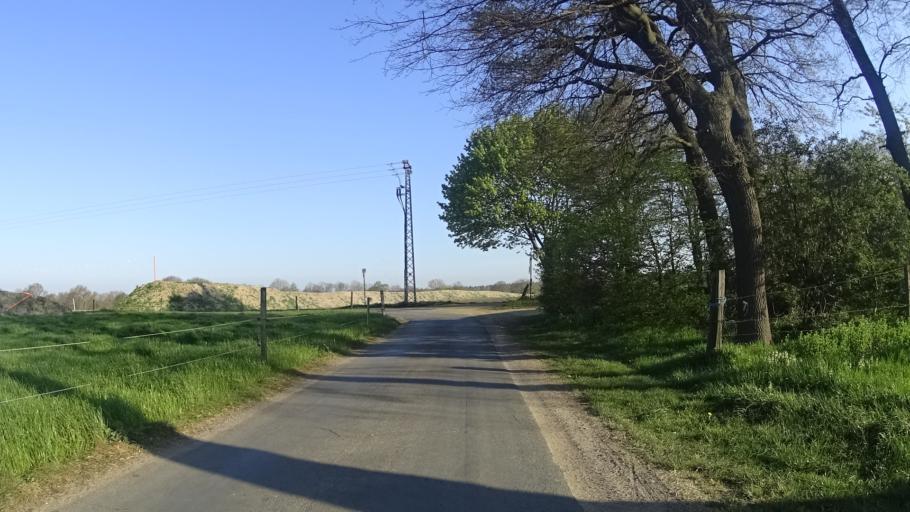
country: DE
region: North Rhine-Westphalia
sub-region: Regierungsbezirk Dusseldorf
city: Voerde
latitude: 51.6403
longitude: 6.7207
